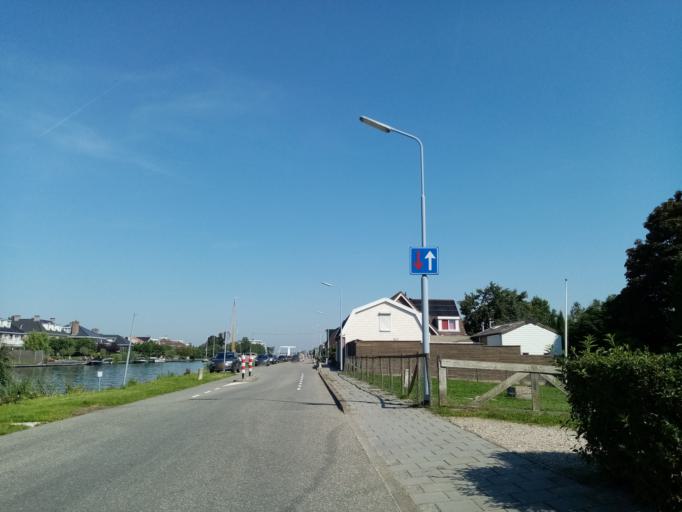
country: NL
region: South Holland
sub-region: Gemeente Lisse
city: Lisse
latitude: 52.2507
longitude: 4.5685
